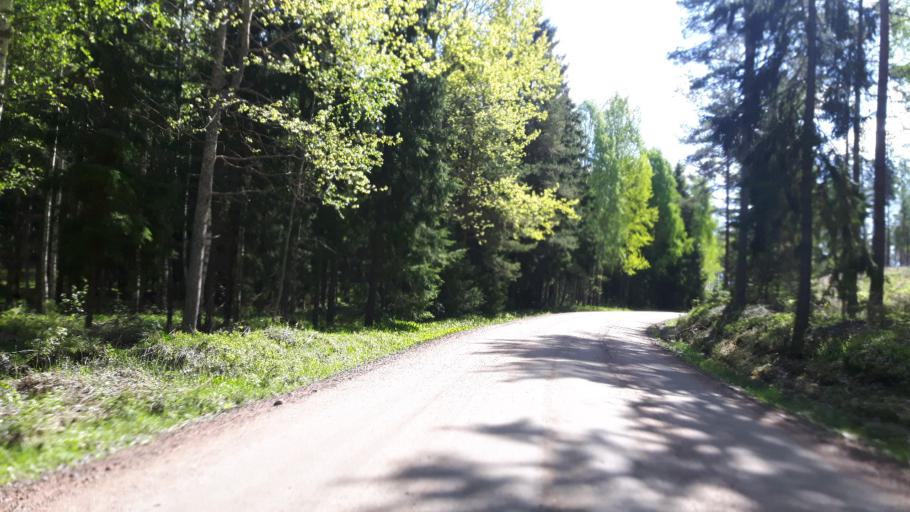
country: FI
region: Kymenlaakso
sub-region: Kotka-Hamina
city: Hamina
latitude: 60.5248
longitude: 27.2754
